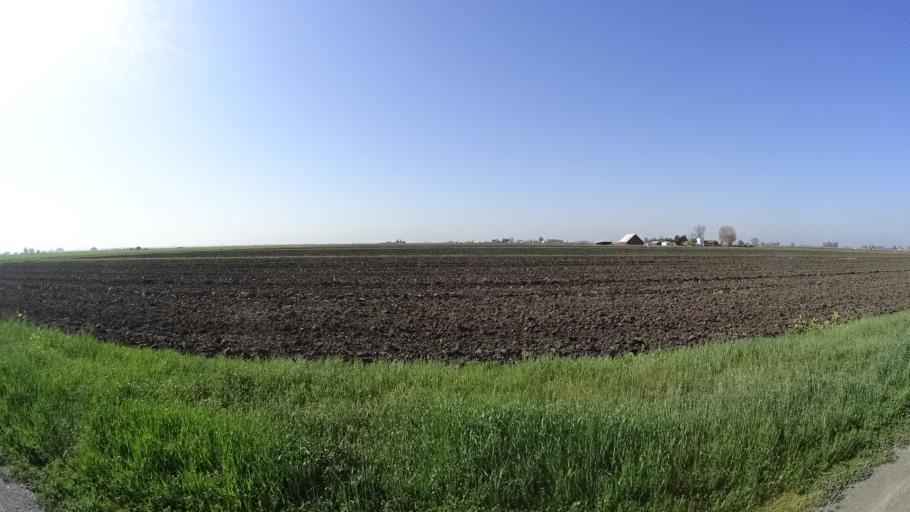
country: US
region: California
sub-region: Glenn County
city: Willows
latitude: 39.5727
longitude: -122.0806
